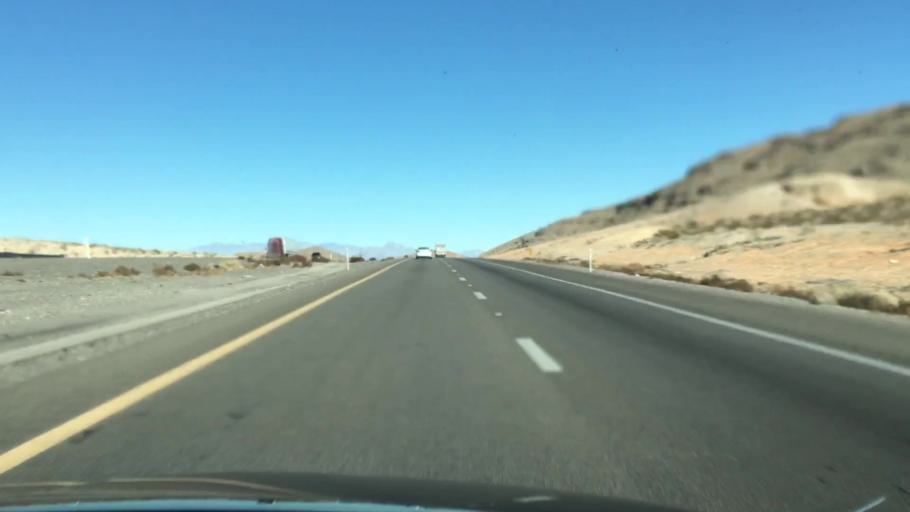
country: US
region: Nevada
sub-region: Clark County
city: Nellis Air Force Base
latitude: 36.4616
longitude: -114.8333
